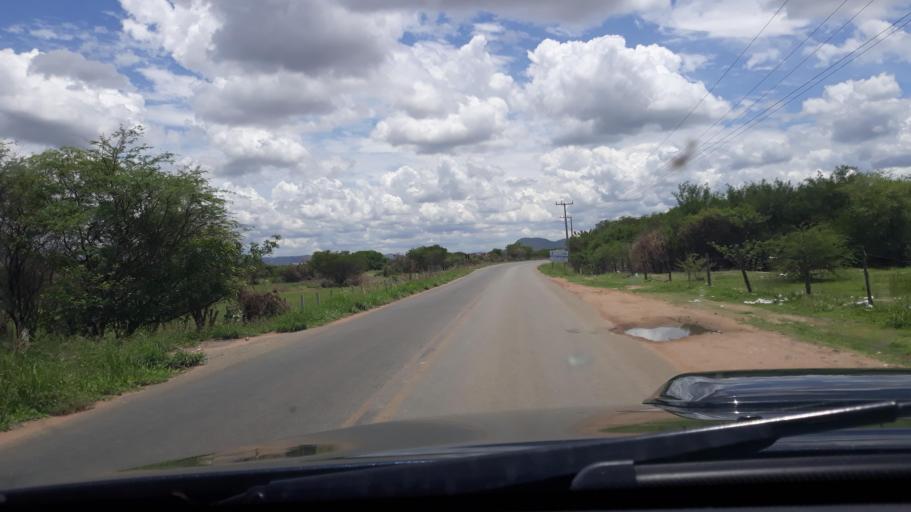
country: BR
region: Bahia
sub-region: Guanambi
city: Guanambi
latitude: -14.1932
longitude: -42.7985
